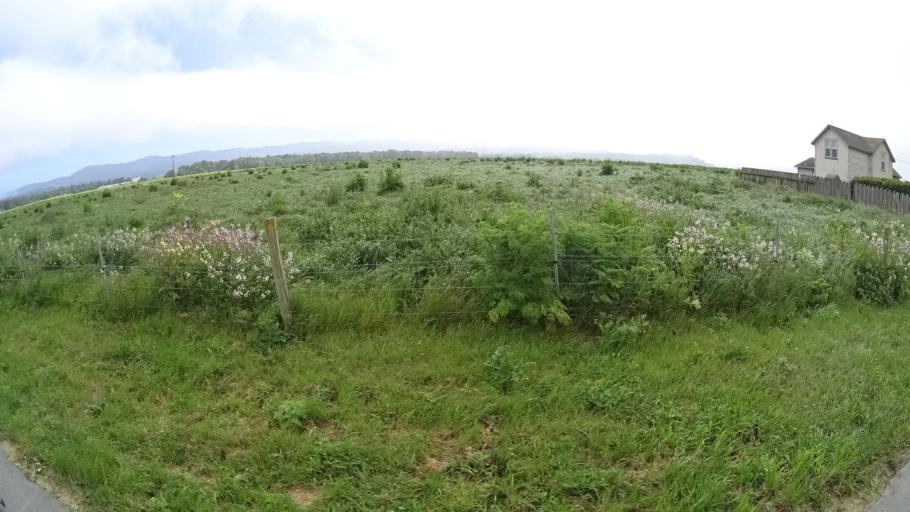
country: US
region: California
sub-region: Humboldt County
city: Fortuna
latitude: 40.5727
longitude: -124.1877
